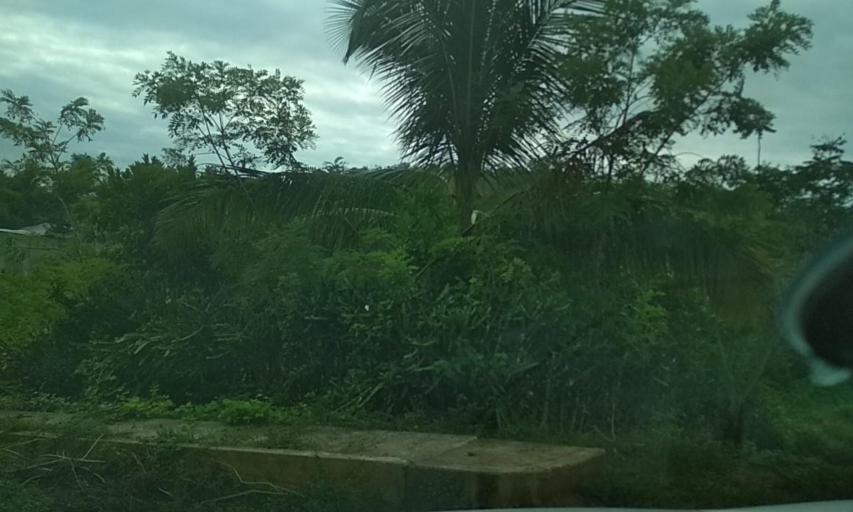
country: MX
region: Veracruz
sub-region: Papantla
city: Polutla
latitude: 20.5824
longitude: -97.2738
